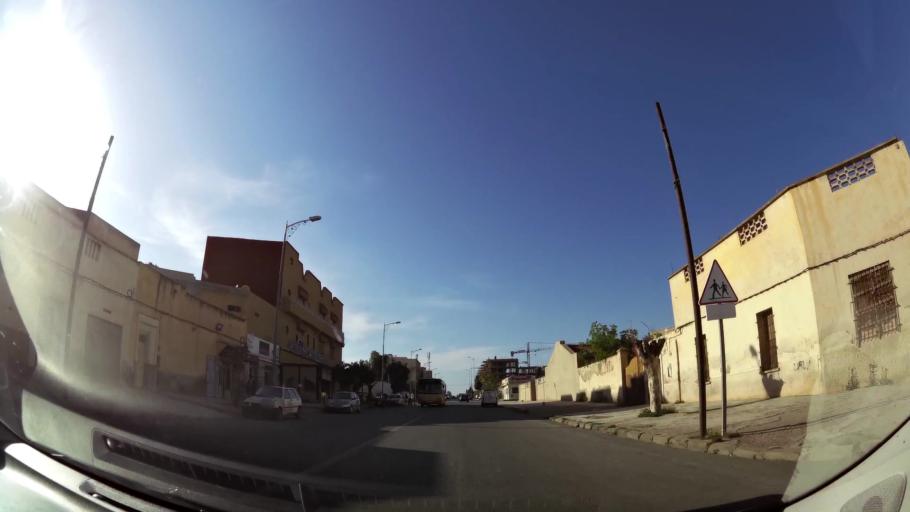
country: MA
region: Oriental
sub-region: Oujda-Angad
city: Oujda
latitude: 34.6929
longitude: -1.9076
